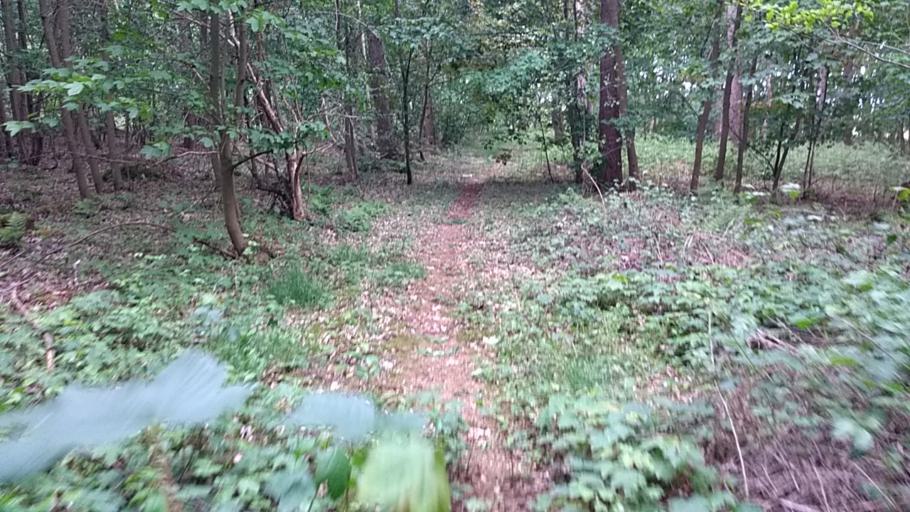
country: NL
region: Limburg
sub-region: Gemeente Leudal
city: Kelpen-Oler
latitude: 51.2843
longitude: 5.8259
